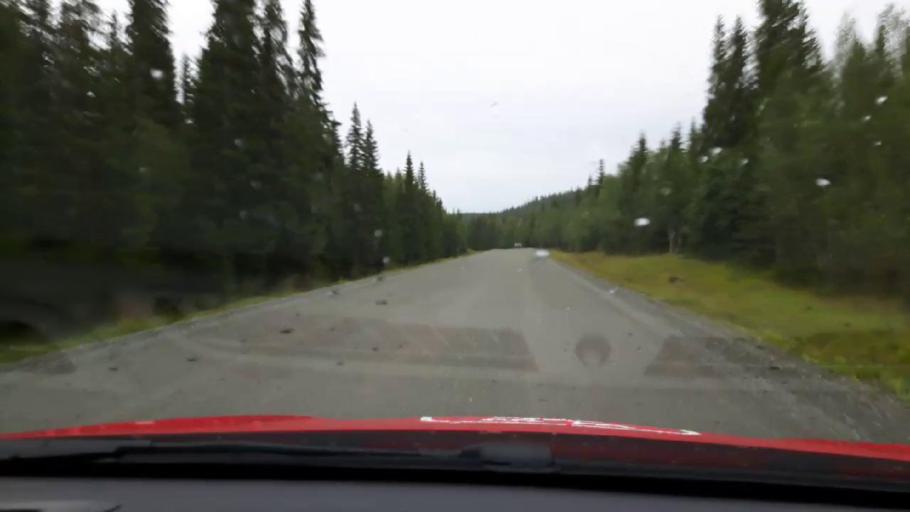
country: SE
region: Jaemtland
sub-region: Are Kommun
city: Are
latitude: 63.4183
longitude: 12.7565
